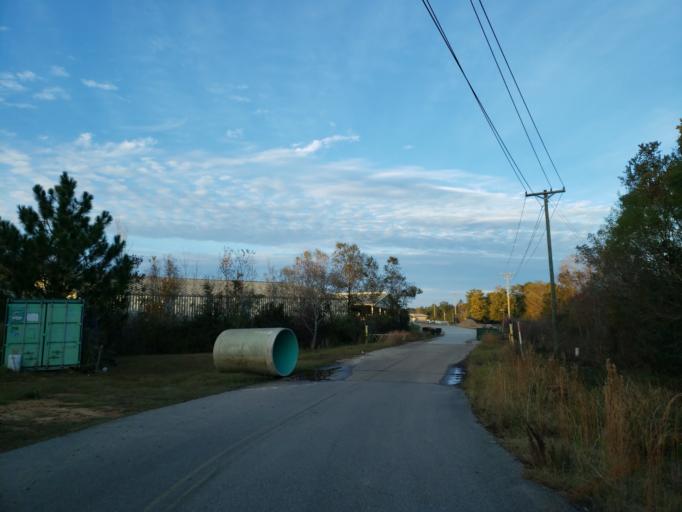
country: US
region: Mississippi
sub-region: Forrest County
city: Hattiesburg
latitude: 31.2558
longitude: -89.2753
